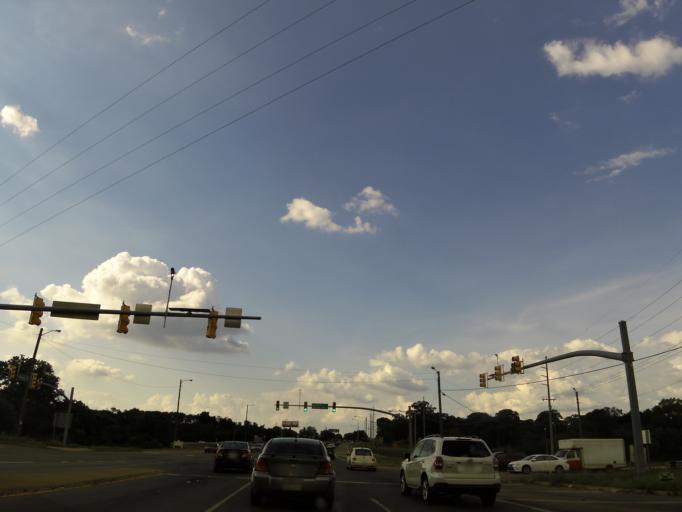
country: US
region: Tennessee
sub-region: Davidson County
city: Lakewood
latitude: 36.2333
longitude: -86.7248
